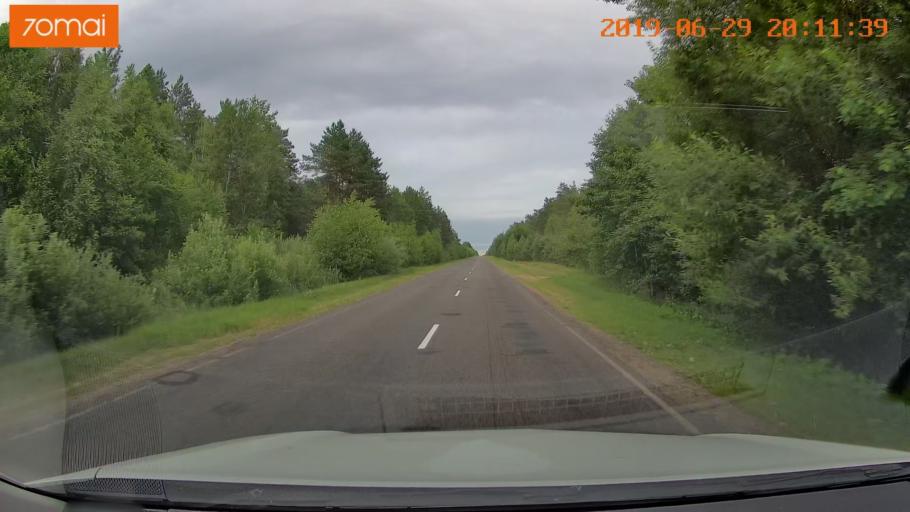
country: BY
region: Brest
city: Lahishyn
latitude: 52.3595
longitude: 26.1182
